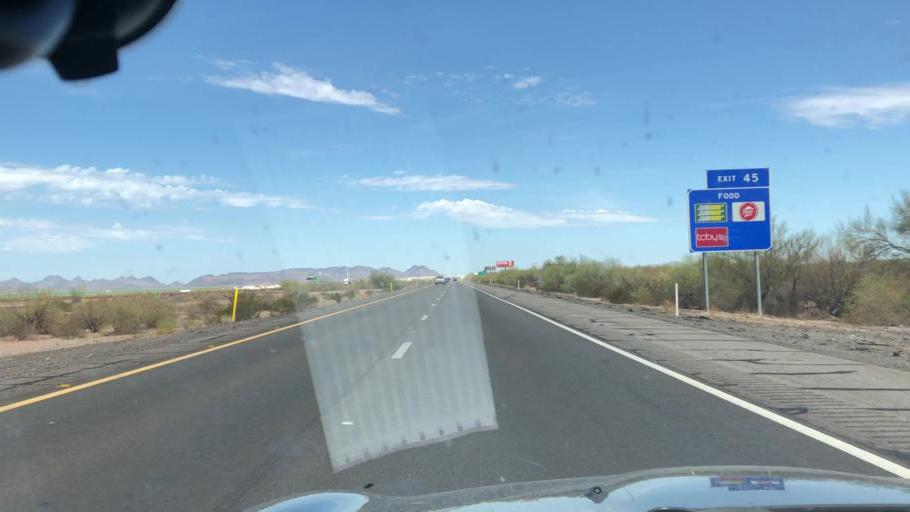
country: US
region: Arizona
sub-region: La Paz County
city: Salome
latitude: 33.6330
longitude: -113.7840
